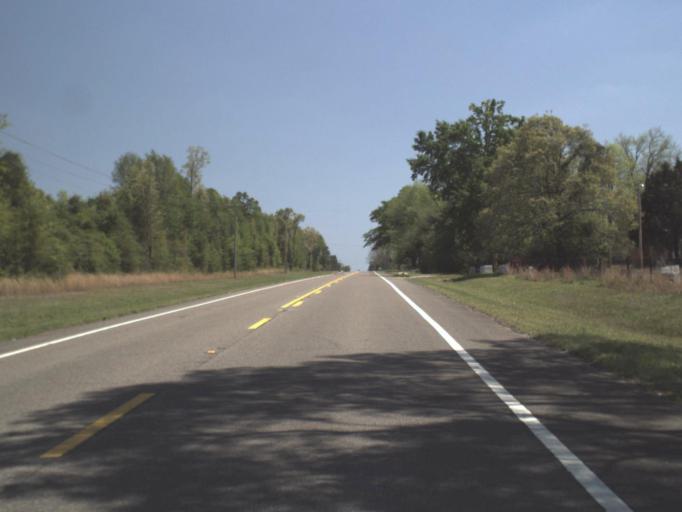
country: US
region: Alabama
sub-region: Escambia County
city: East Brewton
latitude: 30.9402
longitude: -87.0657
